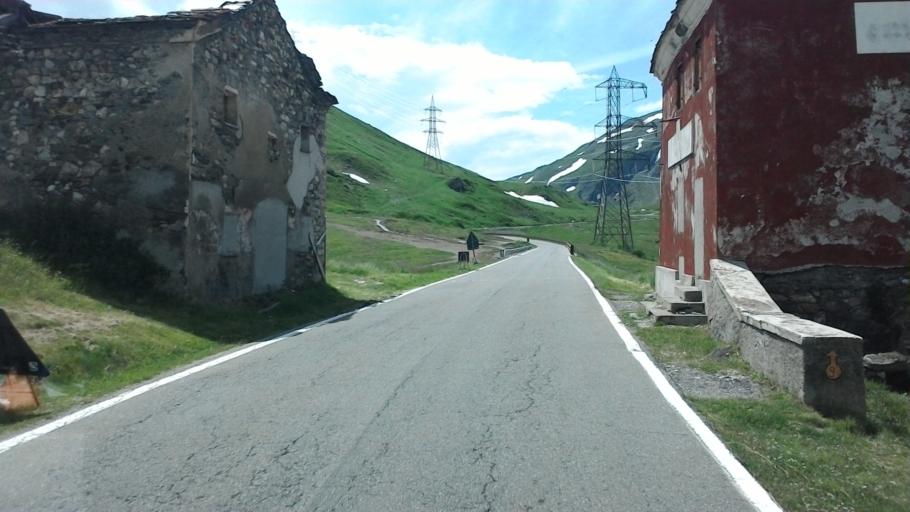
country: IT
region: Aosta Valley
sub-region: Valle d'Aosta
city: La Thuile
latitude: 45.6974
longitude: 6.9014
